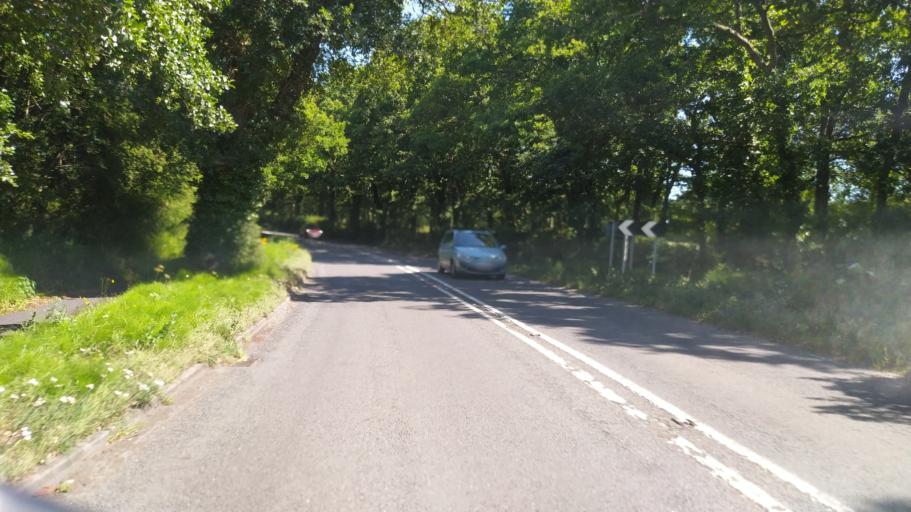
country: GB
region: England
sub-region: Hampshire
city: Cadnam
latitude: 50.9150
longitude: -1.5434
